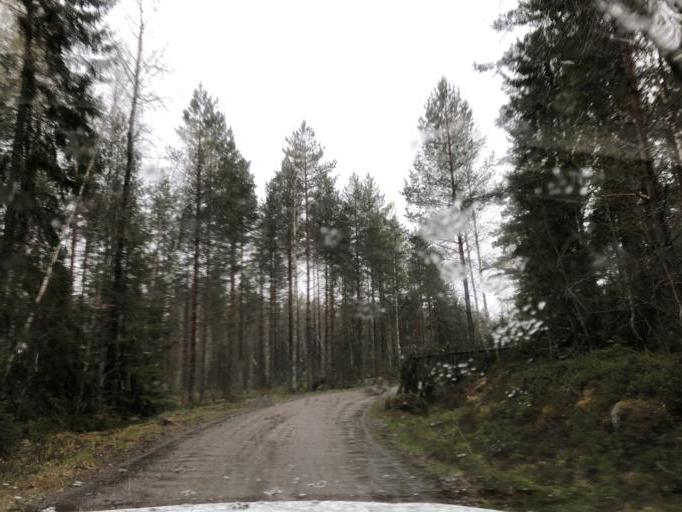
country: SE
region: Uppsala
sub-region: Heby Kommun
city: Tarnsjo
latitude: 60.2094
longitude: 16.8934
